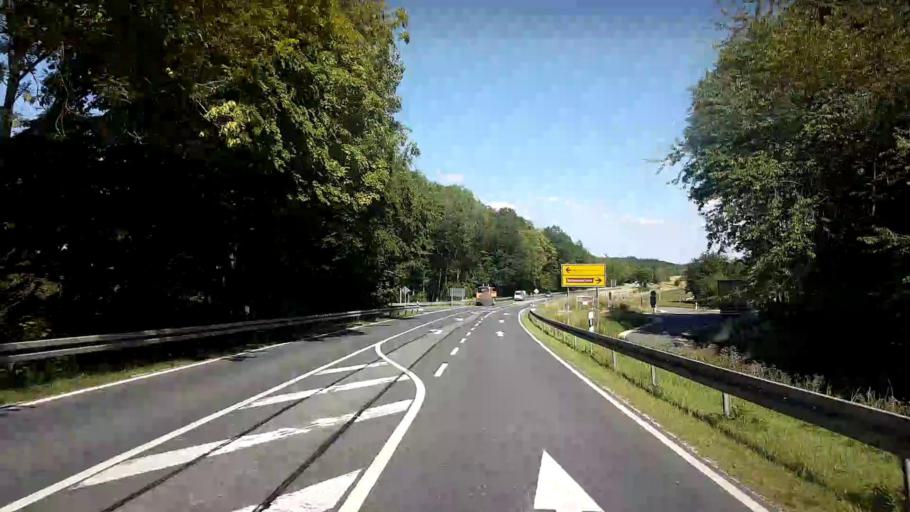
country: DE
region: Bavaria
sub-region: Upper Franconia
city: Ahorn
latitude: 50.2345
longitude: 10.9418
